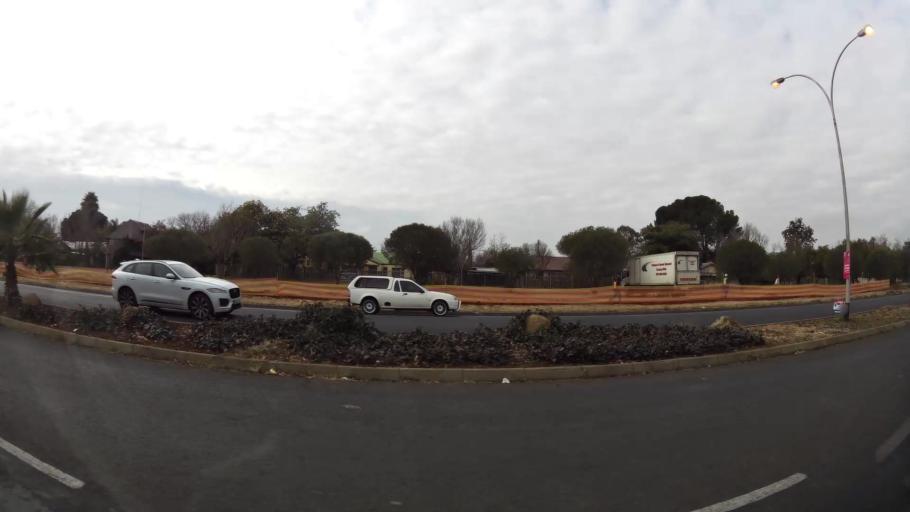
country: ZA
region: Orange Free State
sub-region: Mangaung Metropolitan Municipality
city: Bloemfontein
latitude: -29.1445
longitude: 26.1948
